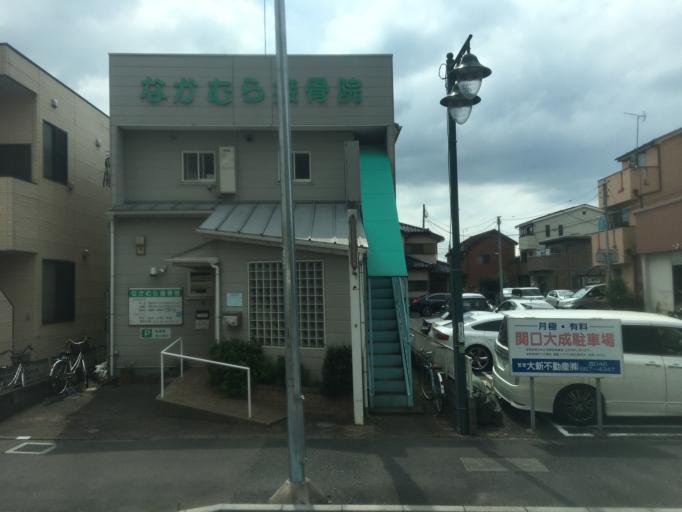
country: JP
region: Saitama
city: Yono
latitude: 35.9160
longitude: 139.6149
